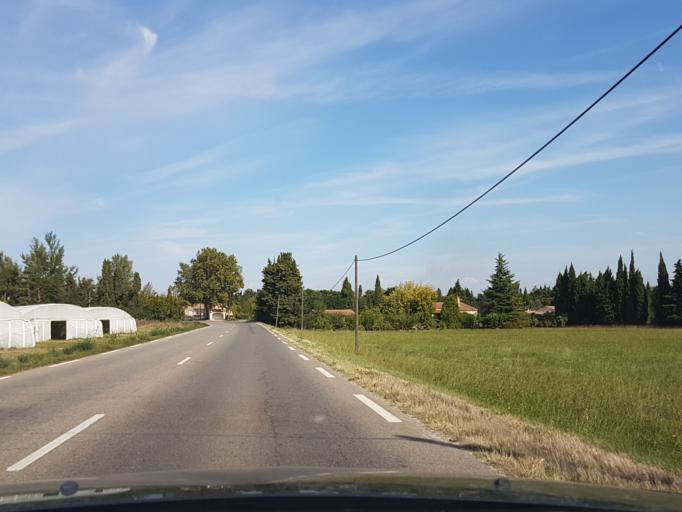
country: FR
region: Provence-Alpes-Cote d'Azur
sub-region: Departement des Bouches-du-Rhone
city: Saint-Remy-de-Provence
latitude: 43.7980
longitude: 4.8567
